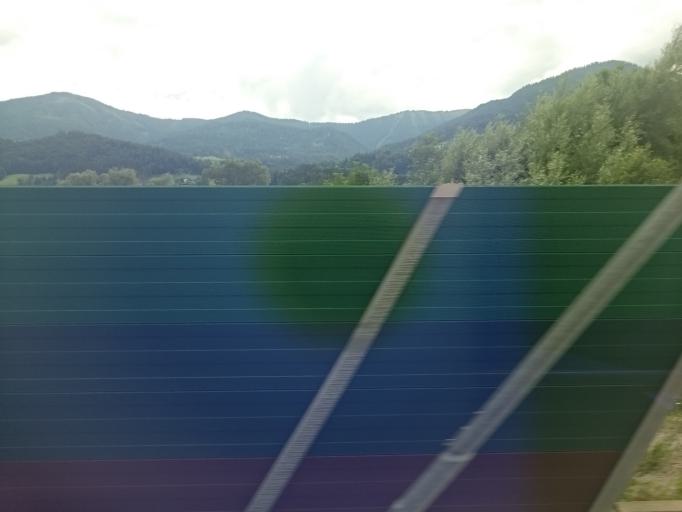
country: AT
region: Tyrol
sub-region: Politischer Bezirk Schwaz
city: Buch bei Jenbach
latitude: 47.3757
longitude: 11.7449
